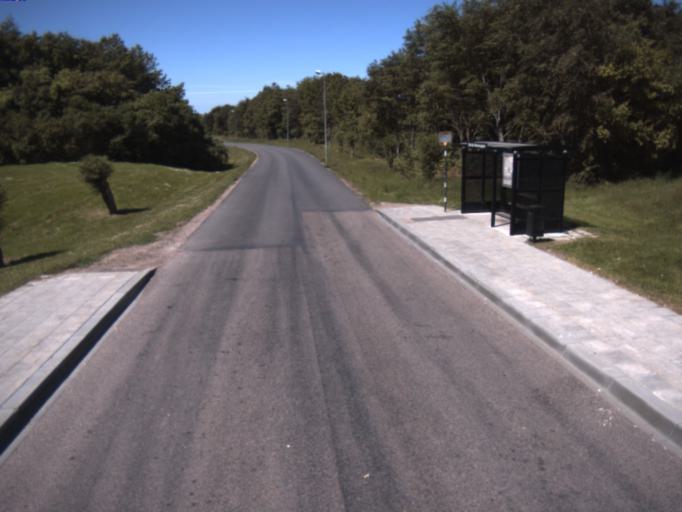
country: SE
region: Skane
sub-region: Helsingborg
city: Barslov
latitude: 56.0096
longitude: 12.8046
